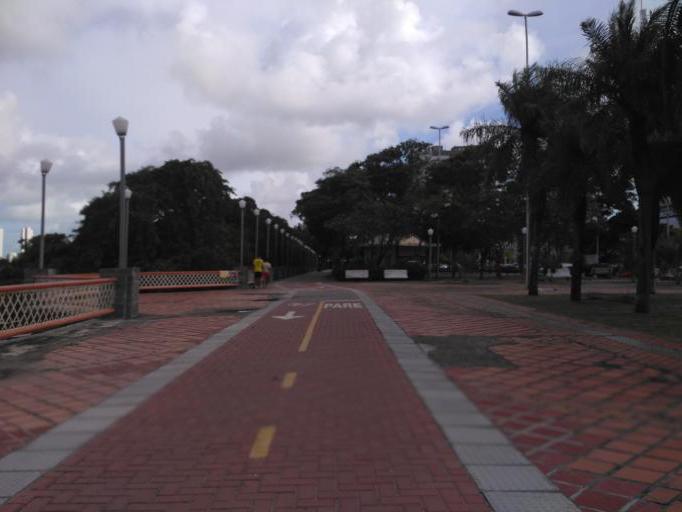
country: BR
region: Pernambuco
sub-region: Recife
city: Recife
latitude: -8.0528
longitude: -34.8753
